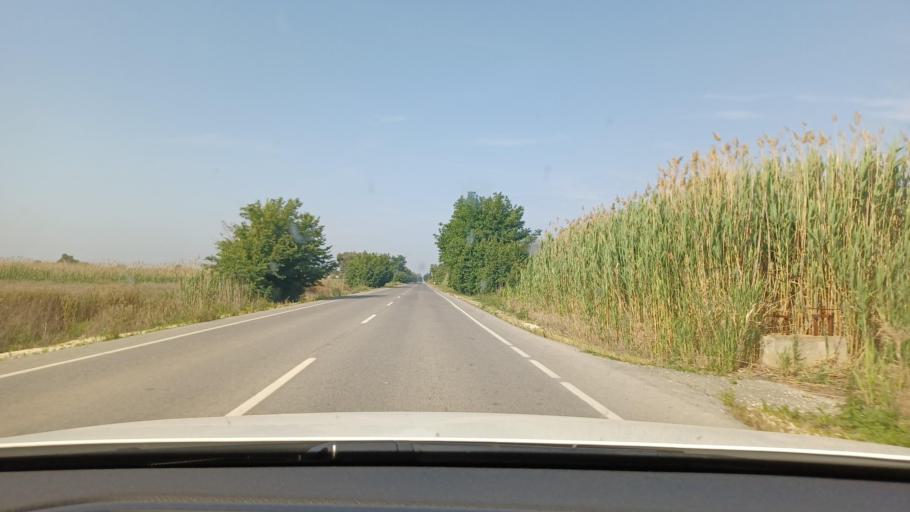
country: ES
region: Valencia
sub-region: Provincia de Alicante
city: Daya Vieja
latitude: 38.1566
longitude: -0.7070
